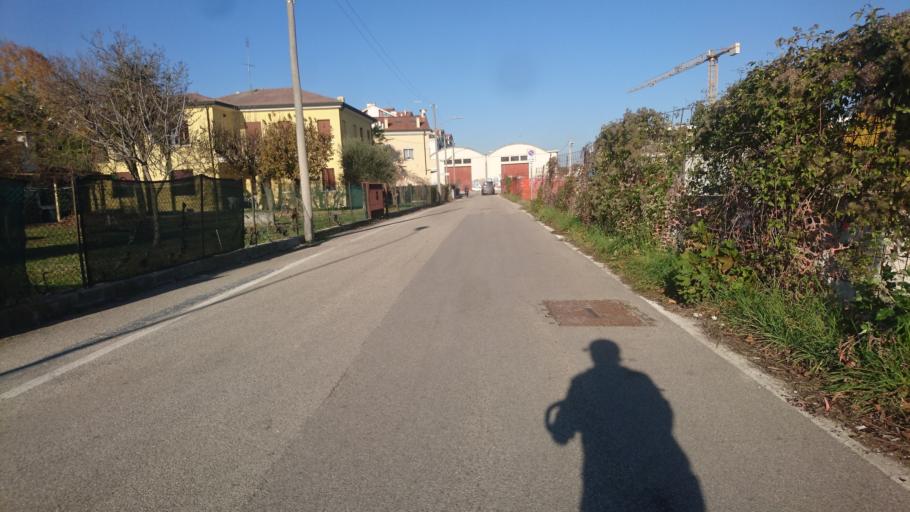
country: IT
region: Veneto
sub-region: Provincia di Padova
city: Caselle
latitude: 45.4067
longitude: 11.8480
